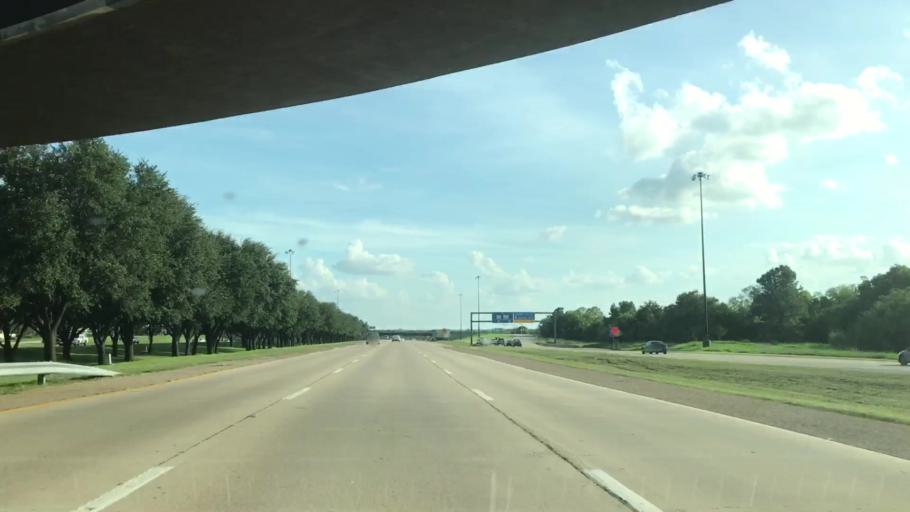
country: US
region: Texas
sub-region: Tarrant County
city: Euless
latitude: 32.8574
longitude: -97.0410
